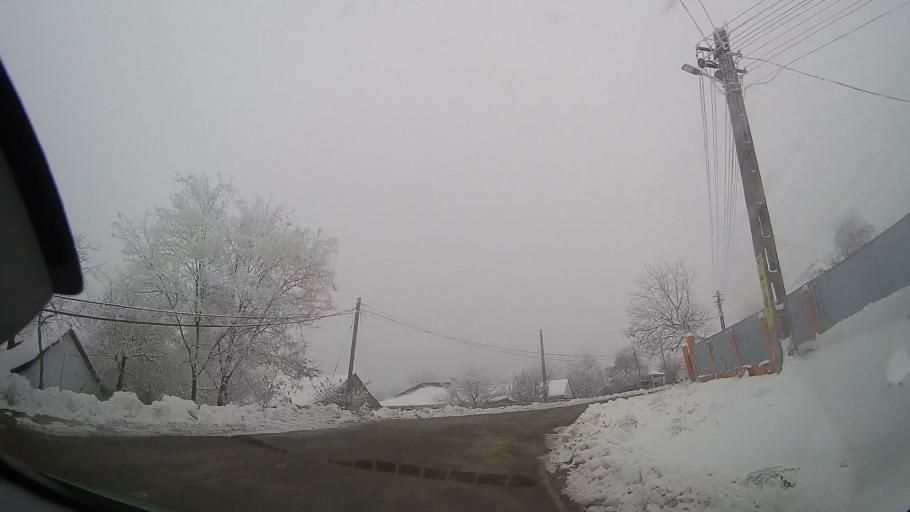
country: RO
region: Neamt
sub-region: Comuna Valea Ursului
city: Valea Ursului
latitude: 46.8007
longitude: 27.0818
